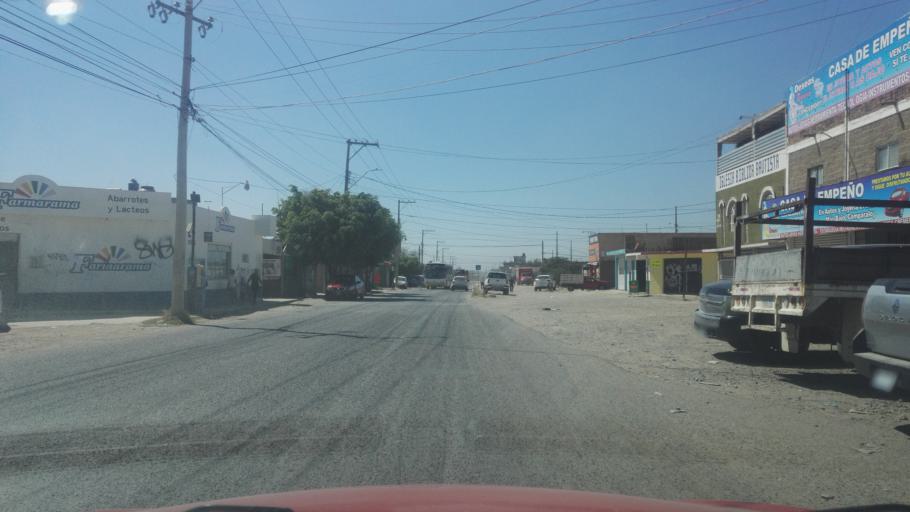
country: MX
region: Guanajuato
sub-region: Leon
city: Fraccionamiento Paraiso Real
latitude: 21.0944
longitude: -101.5913
